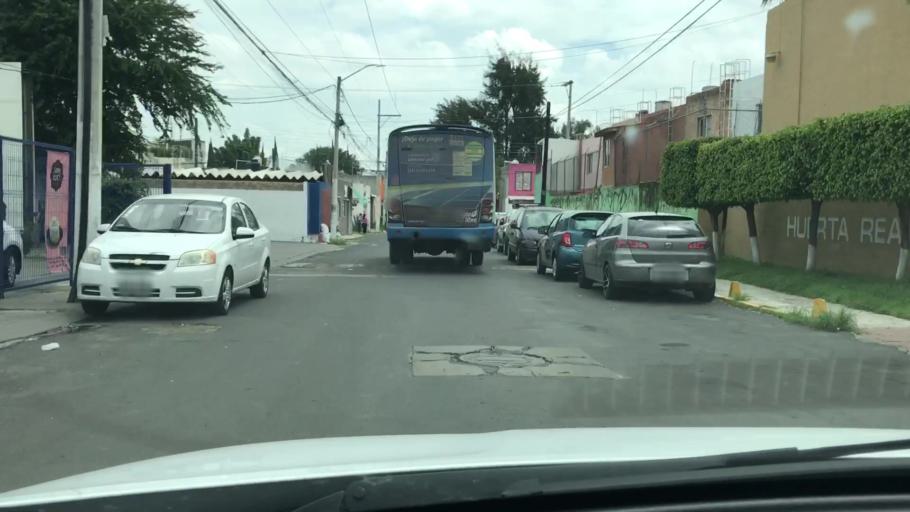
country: MX
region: Jalisco
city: Guadalajara
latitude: 20.6442
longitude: -103.4347
